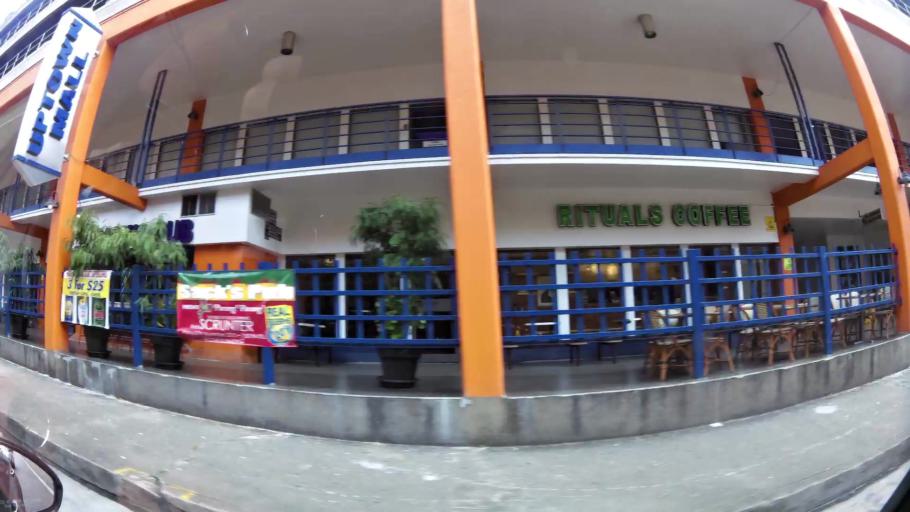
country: TT
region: City of Port of Spain
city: Port-of-Spain
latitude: 10.6556
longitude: -61.5130
